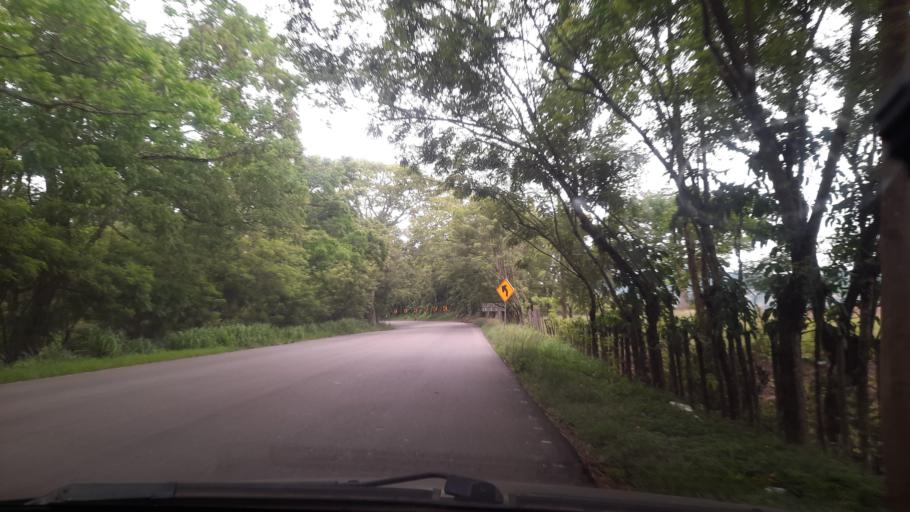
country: GT
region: Izabal
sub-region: Municipio de Los Amates
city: Los Amates
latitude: 15.2509
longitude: -89.1248
